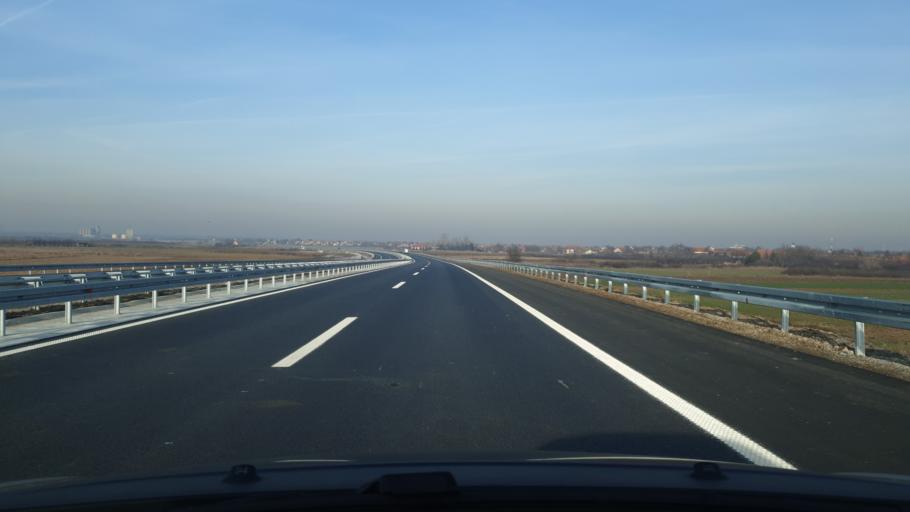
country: RS
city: Boljevci
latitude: 44.7445
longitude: 20.2487
